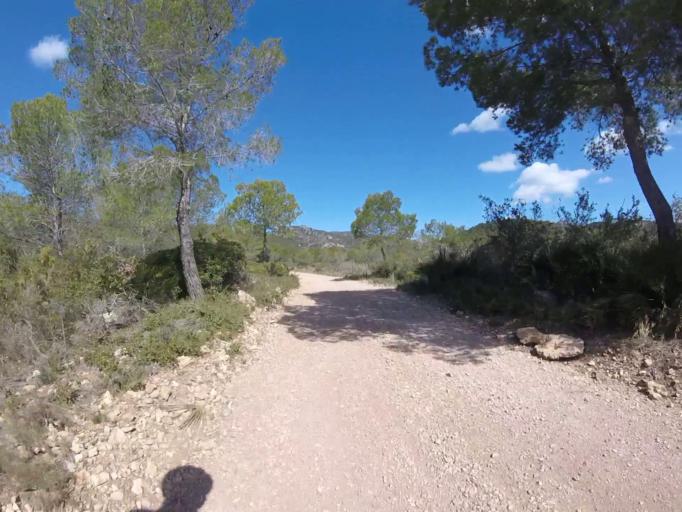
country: ES
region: Valencia
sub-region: Provincia de Castello
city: Alcoceber
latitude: 40.2879
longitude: 0.3189
